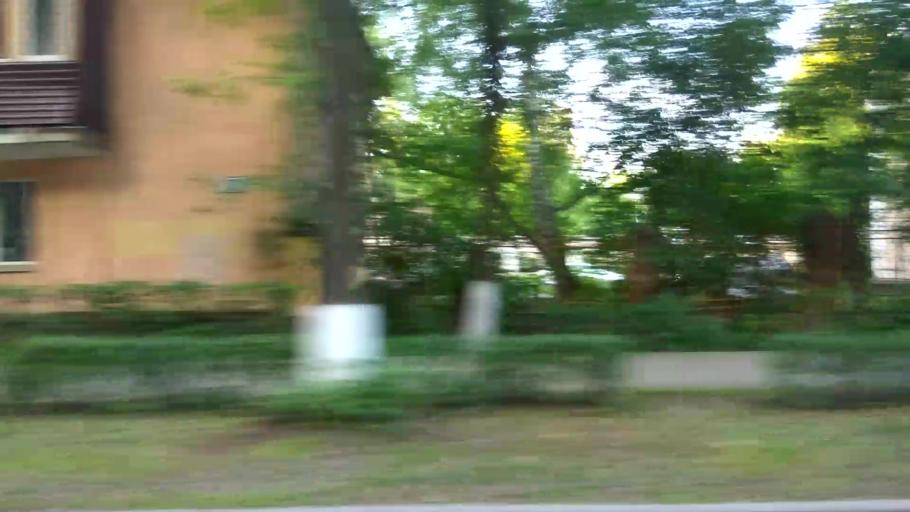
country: RU
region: Moskovskaya
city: Korolev
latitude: 55.9228
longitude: 37.8194
